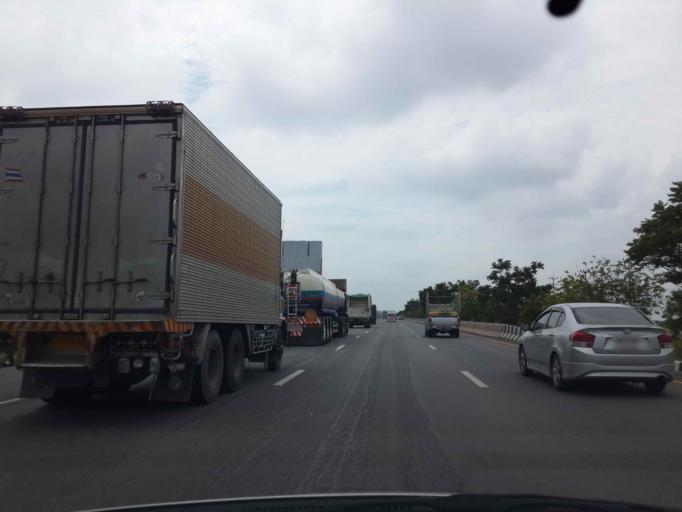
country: TH
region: Samut Songkhram
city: Samut Songkhram
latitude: 13.4376
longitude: 100.0598
